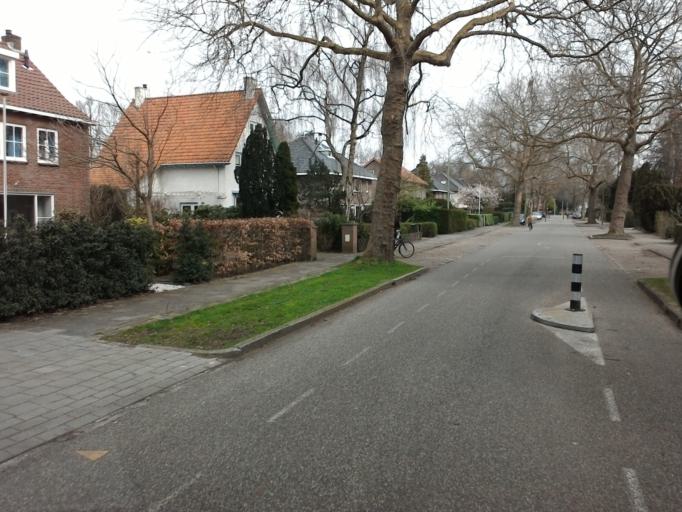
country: NL
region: Utrecht
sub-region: Gemeente Zeist
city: Zeist
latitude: 52.0821
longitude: 5.2305
